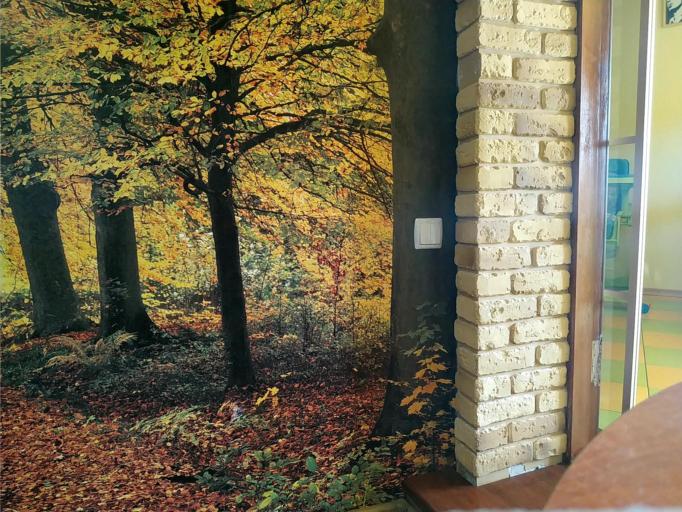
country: RU
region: Smolensk
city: Katyn'
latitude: 54.9772
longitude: 31.7319
